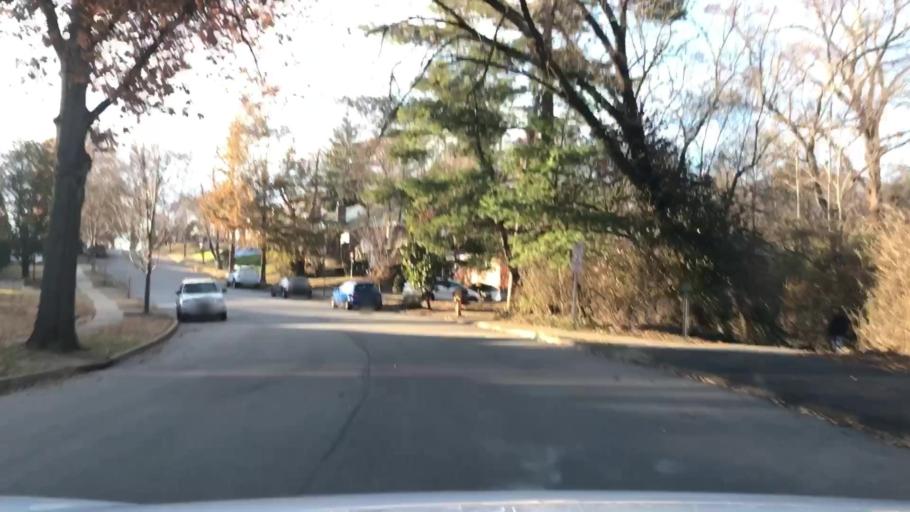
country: US
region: Missouri
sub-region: Saint Louis County
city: Brentwood
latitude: 38.6187
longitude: -90.3388
